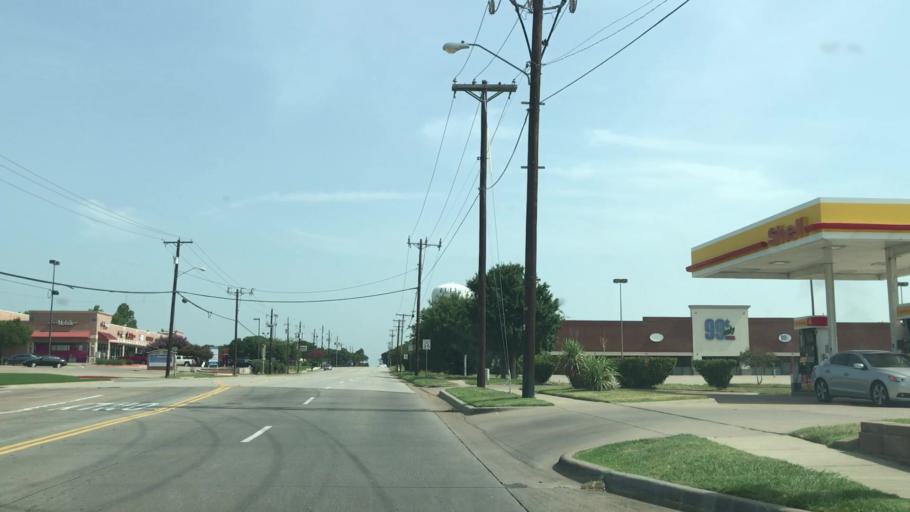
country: US
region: Texas
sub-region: Tarrant County
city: Euless
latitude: 32.8519
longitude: -97.0825
